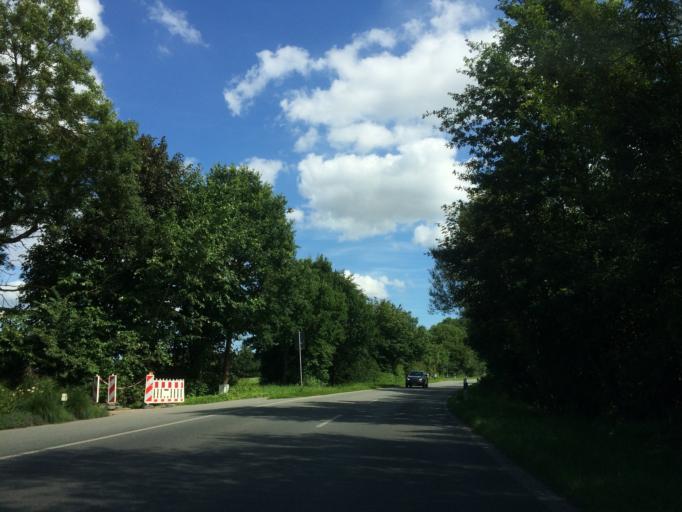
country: DE
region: Schleswig-Holstein
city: Malente
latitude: 54.1638
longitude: 10.5694
